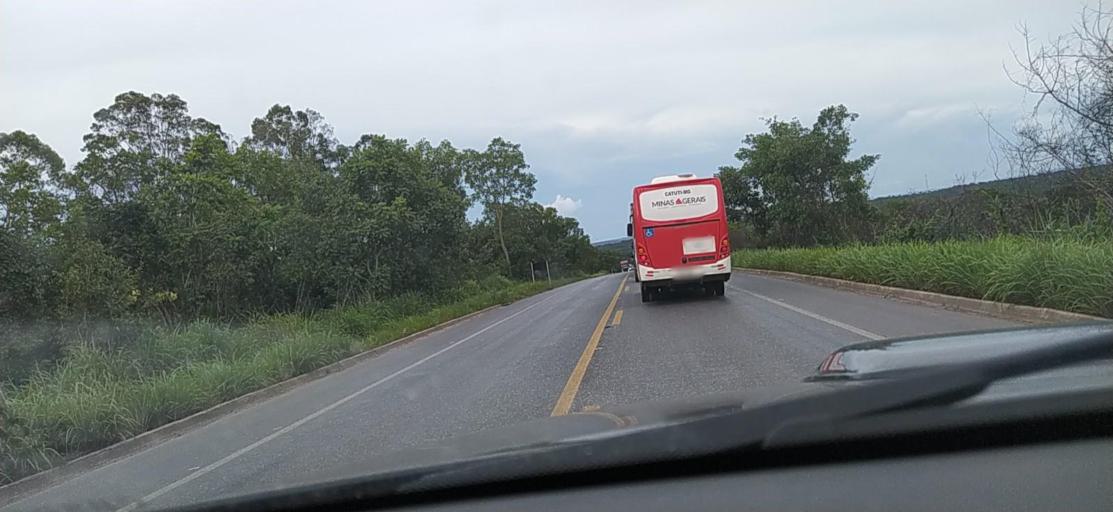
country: BR
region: Minas Gerais
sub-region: Montes Claros
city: Montes Claros
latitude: -16.6686
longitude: -43.7896
